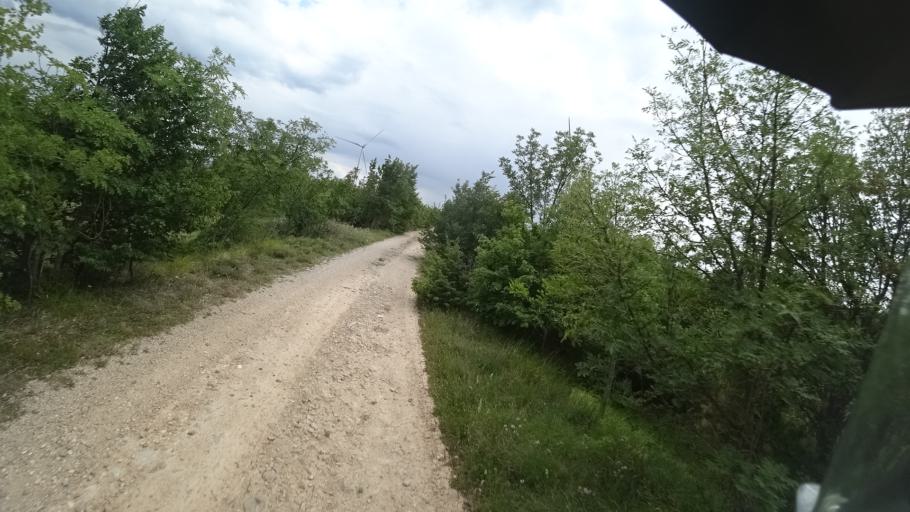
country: HR
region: Sibensko-Kniniska
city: Knin
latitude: 44.0948
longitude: 16.0753
